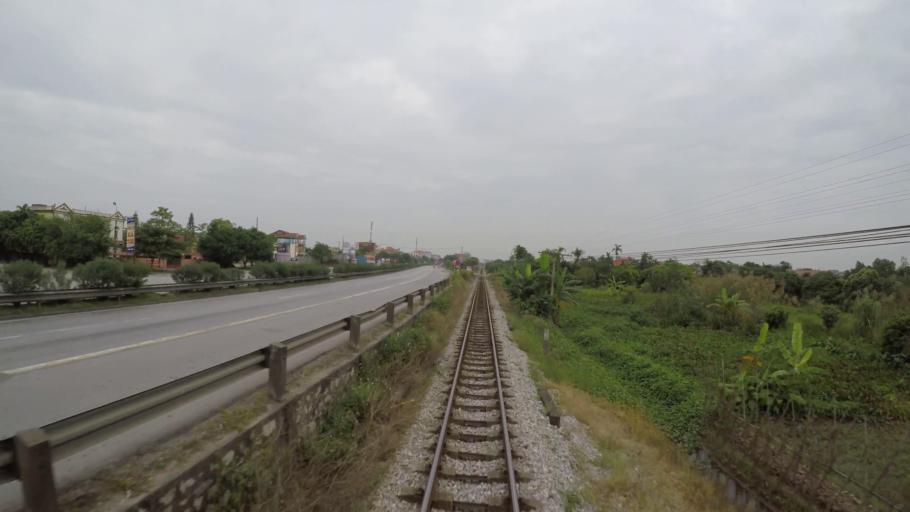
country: VN
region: Hai Duong
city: Phu Thai
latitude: 20.9749
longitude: 106.4354
